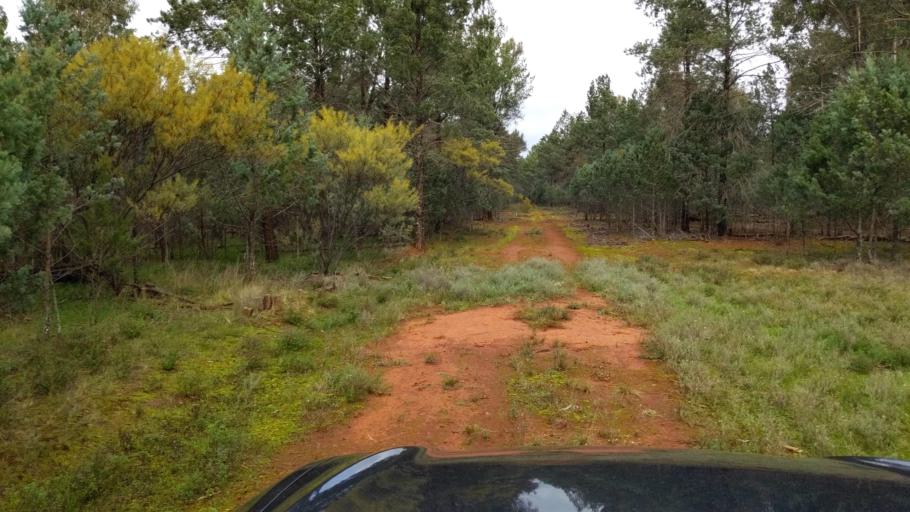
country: AU
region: New South Wales
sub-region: Coolamon
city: Coolamon
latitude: -34.8269
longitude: 146.9362
